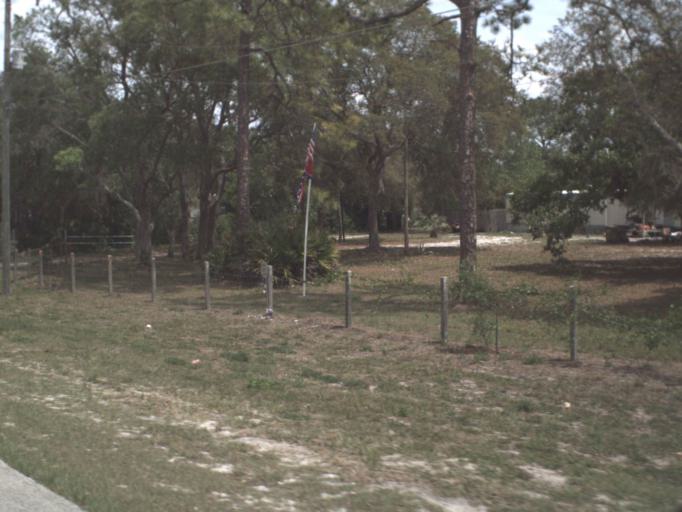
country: US
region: Florida
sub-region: Lake County
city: Lake Mack-Forest Hills
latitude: 28.9671
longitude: -81.4105
